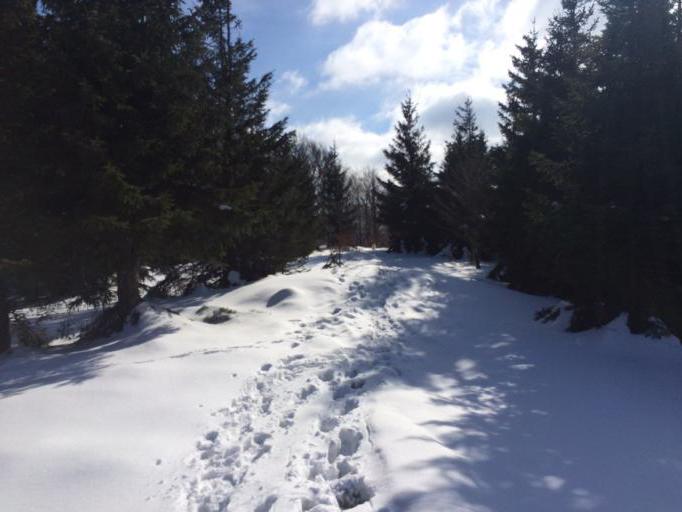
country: CZ
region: Olomoucky
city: Vapenna
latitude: 50.2643
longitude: 17.0133
